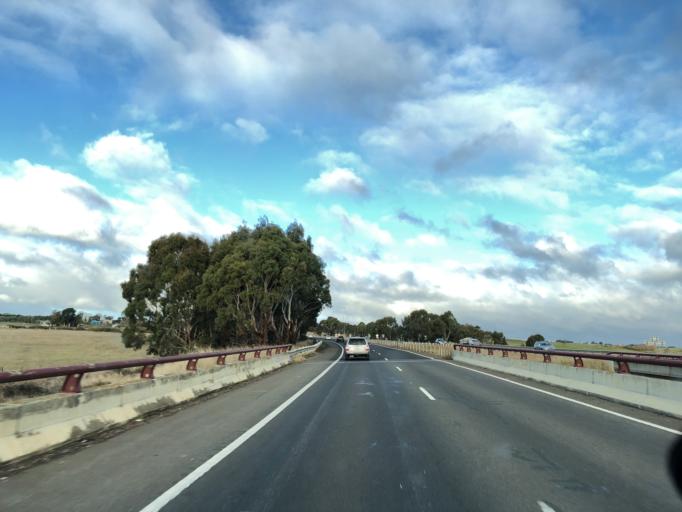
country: AU
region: Victoria
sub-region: Mount Alexander
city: Castlemaine
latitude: -37.2221
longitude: 144.4189
